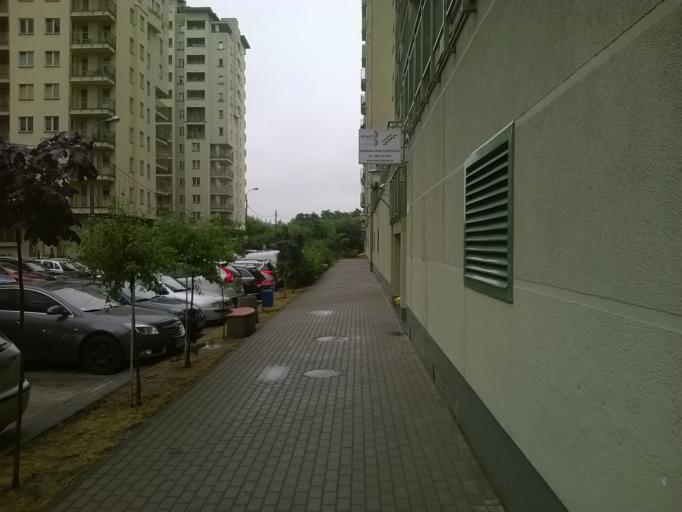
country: PL
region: Masovian Voivodeship
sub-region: Warszawa
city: Mokotow
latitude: 52.1811
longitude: 21.0269
